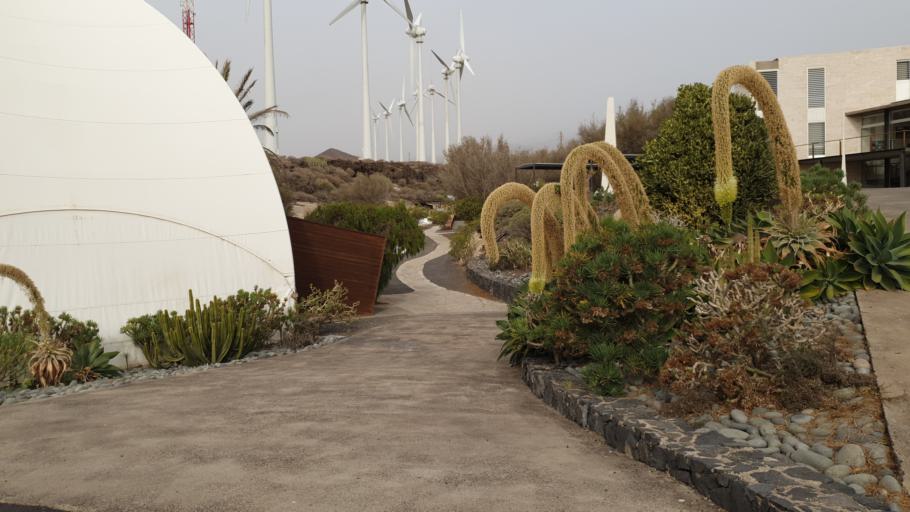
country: ES
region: Canary Islands
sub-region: Provincia de Santa Cruz de Tenerife
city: San Isidro
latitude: 28.0700
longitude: -16.5133
